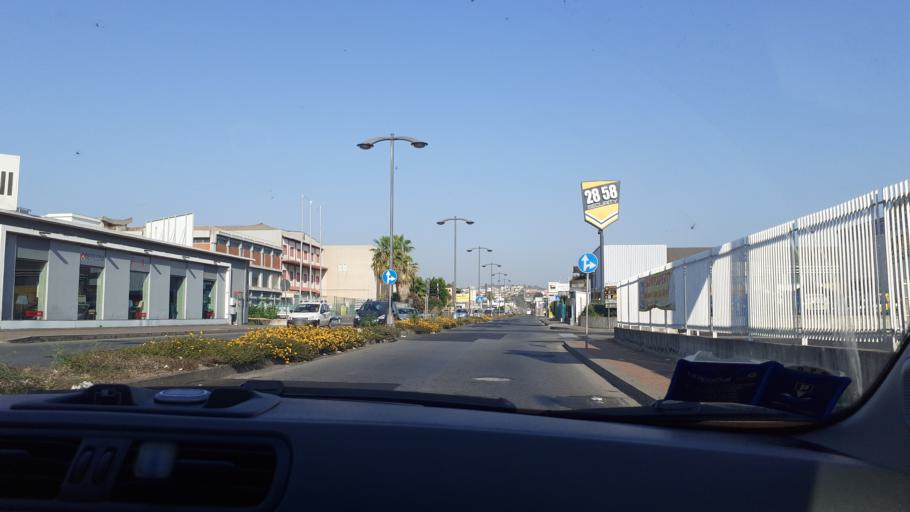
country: IT
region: Sicily
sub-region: Catania
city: Misterbianco
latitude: 37.5118
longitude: 15.0324
